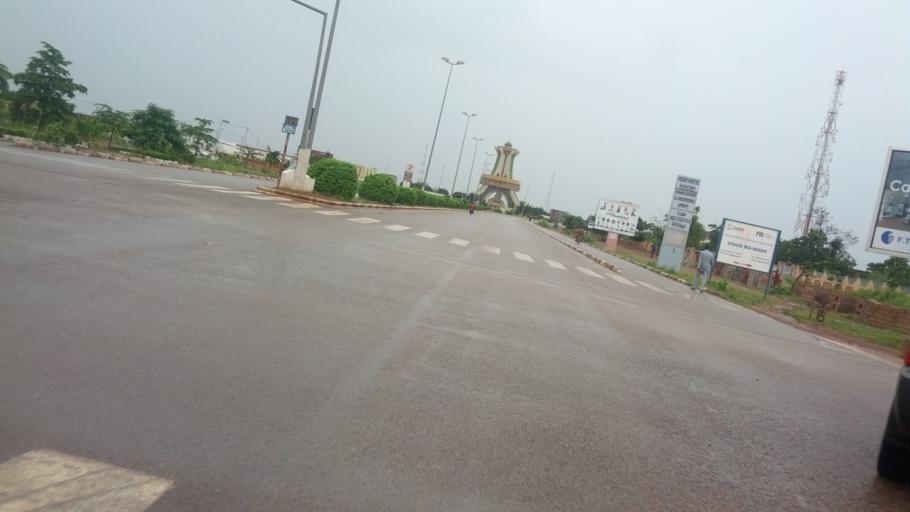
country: BF
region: Centre
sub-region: Kadiogo Province
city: Ouagadougou
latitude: 12.3179
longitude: -1.5027
